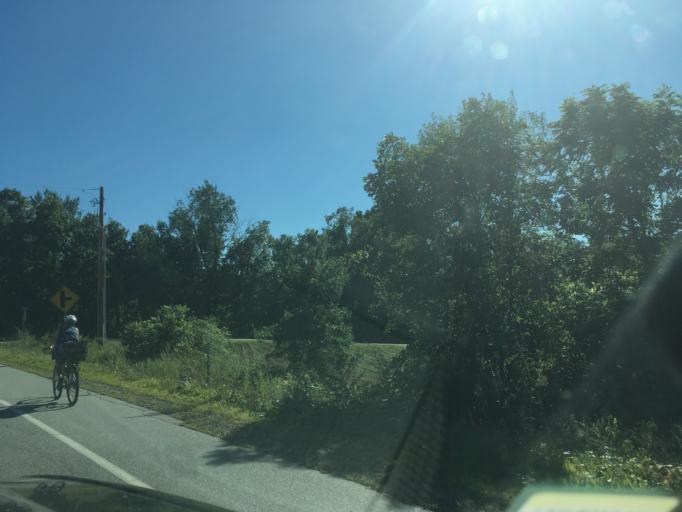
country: US
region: New Hampshire
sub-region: Rockingham County
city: Stratham Station
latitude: 43.0162
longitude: -70.9167
